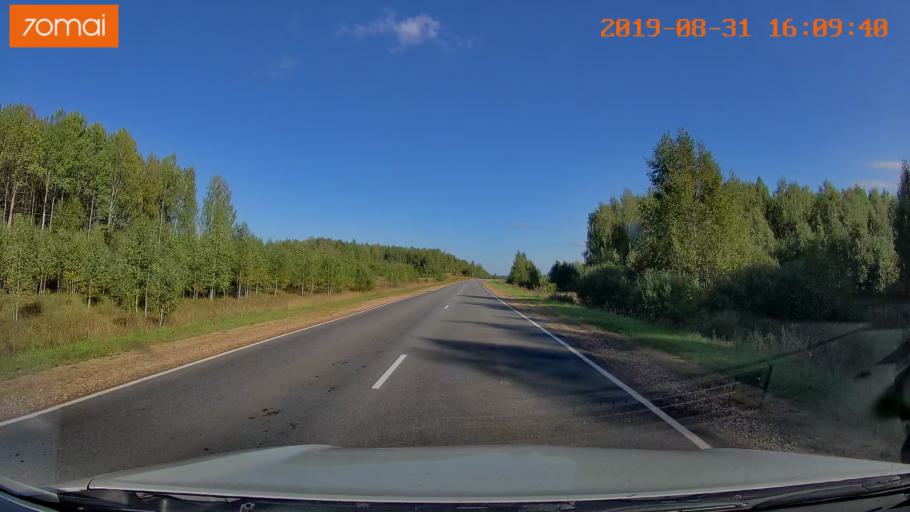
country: RU
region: Kaluga
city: Yukhnov
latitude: 54.5876
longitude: 35.4050
